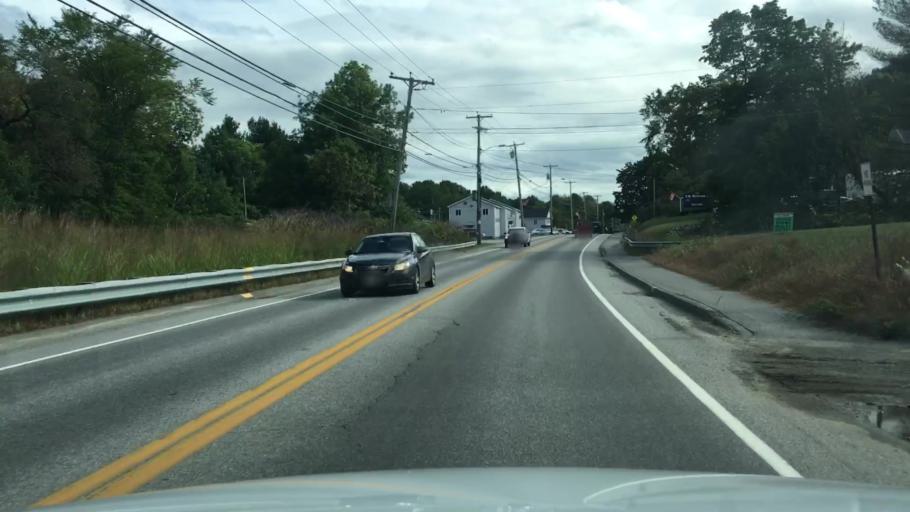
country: US
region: Maine
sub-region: Kennebec County
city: Farmingdale
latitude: 44.2467
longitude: -69.7709
